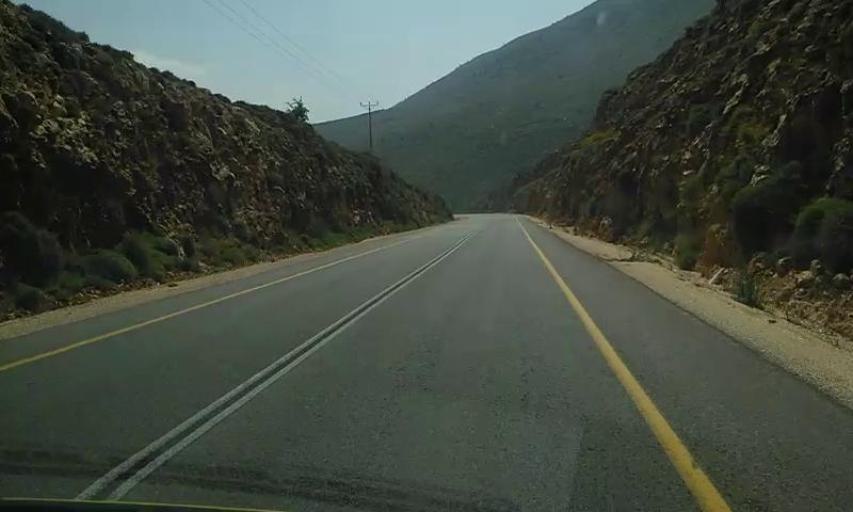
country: PS
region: West Bank
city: Majdal Bani Fadil
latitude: 32.0772
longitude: 35.3525
